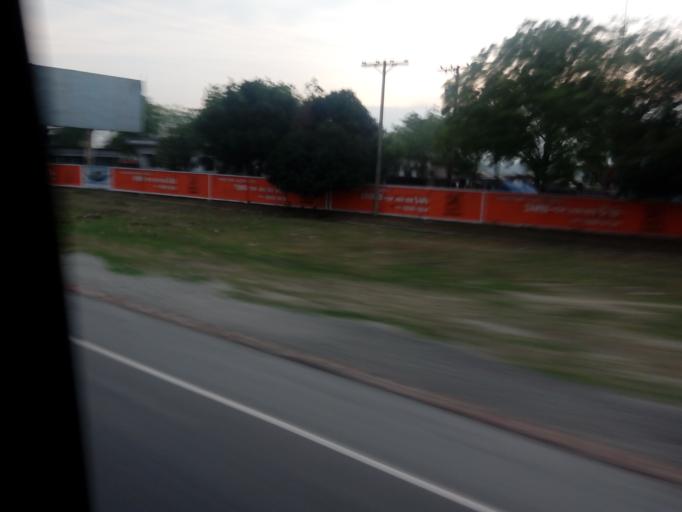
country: BD
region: Rajshahi
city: Sirajganj
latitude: 24.3956
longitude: 89.7344
